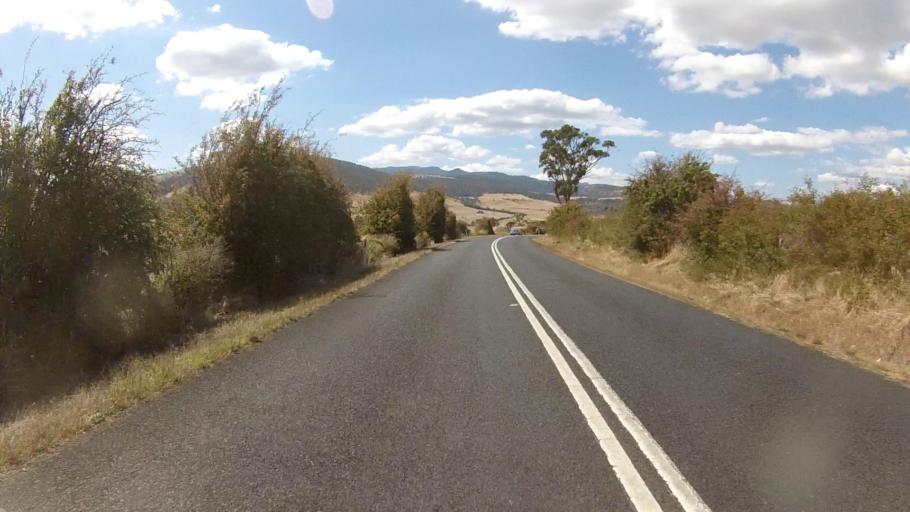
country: AU
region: Tasmania
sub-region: Derwent Valley
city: New Norfolk
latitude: -42.7362
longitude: 146.9377
